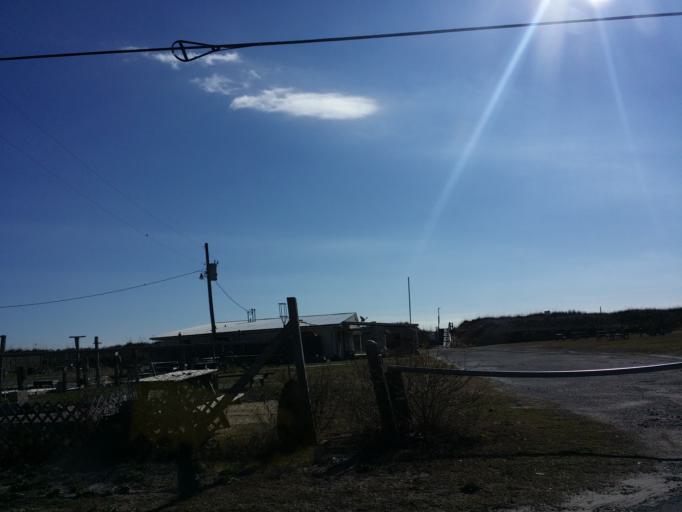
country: US
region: North Carolina
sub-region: Pender County
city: Surf City
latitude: 34.4519
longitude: -77.5024
